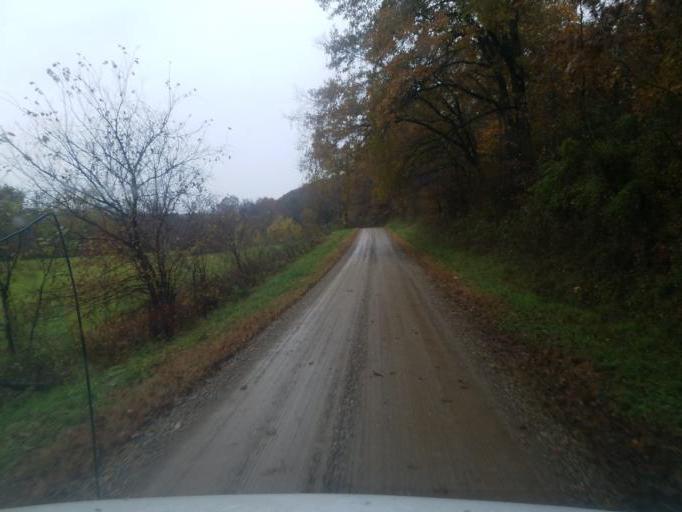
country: US
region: Ohio
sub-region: Washington County
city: Beverly
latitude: 39.4582
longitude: -81.7735
